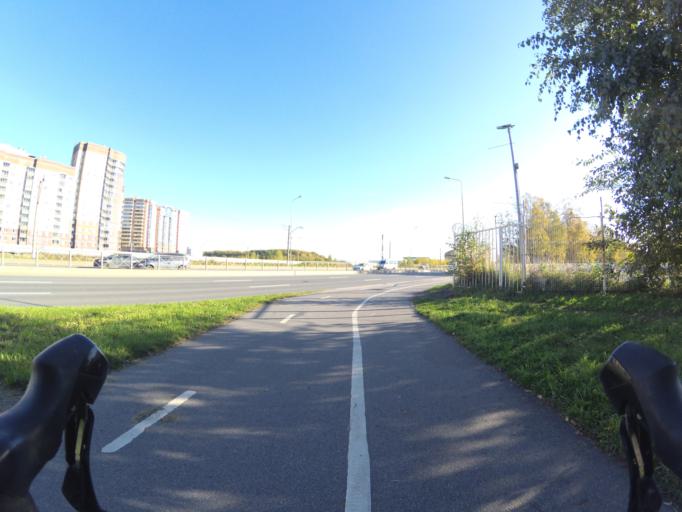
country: RU
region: Leningrad
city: Untolovo
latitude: 59.9939
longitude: 30.2127
